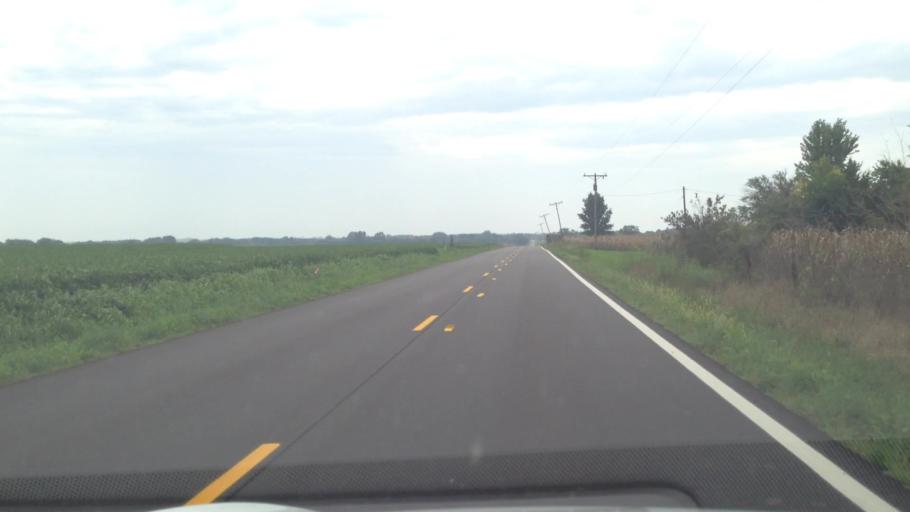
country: US
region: Kansas
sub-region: Crawford County
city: Girard
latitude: 37.6228
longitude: -94.9698
